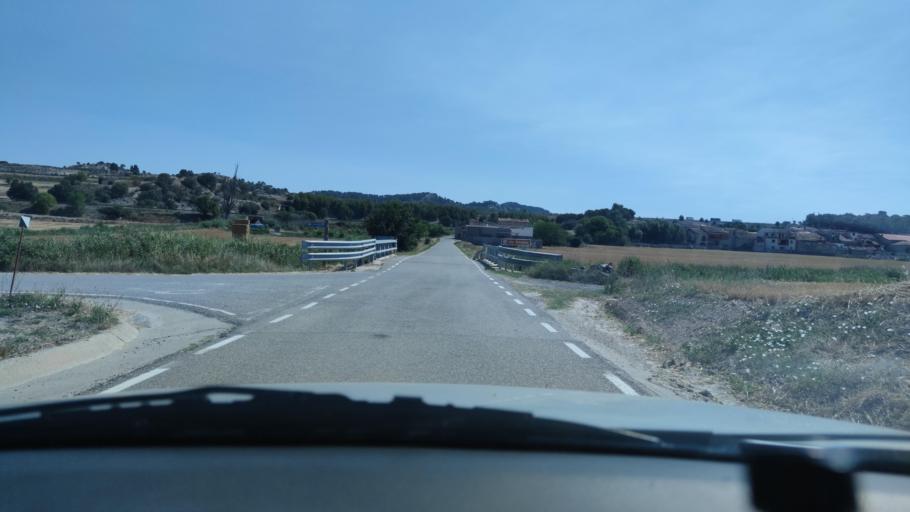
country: ES
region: Catalonia
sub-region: Provincia de Lleida
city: Cervera
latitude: 41.6330
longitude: 1.3327
